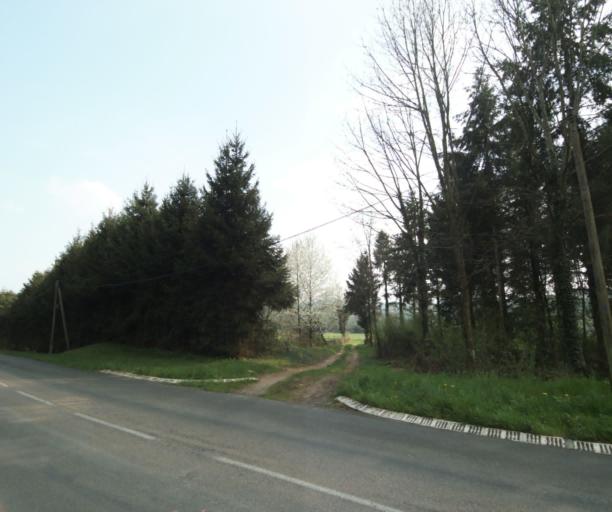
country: FR
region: Bourgogne
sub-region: Departement de Saone-et-Loire
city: Charolles
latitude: 46.4900
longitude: 4.4298
